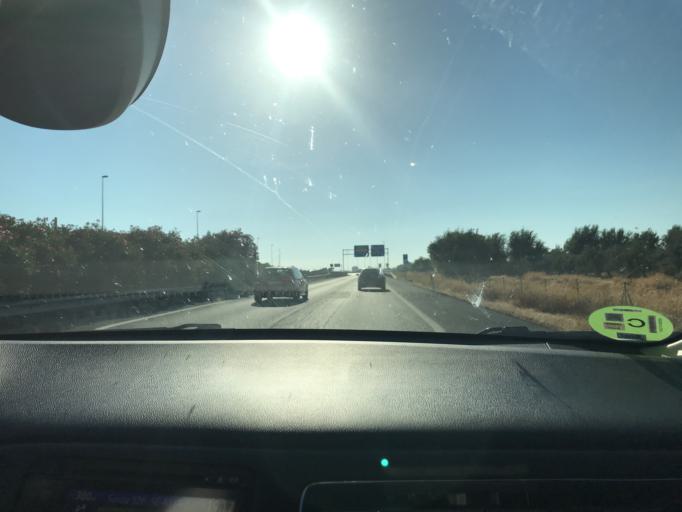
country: ES
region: Andalusia
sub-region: Provincia de Sevilla
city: Alcala de Guadaira
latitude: 37.4320
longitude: -5.8296
